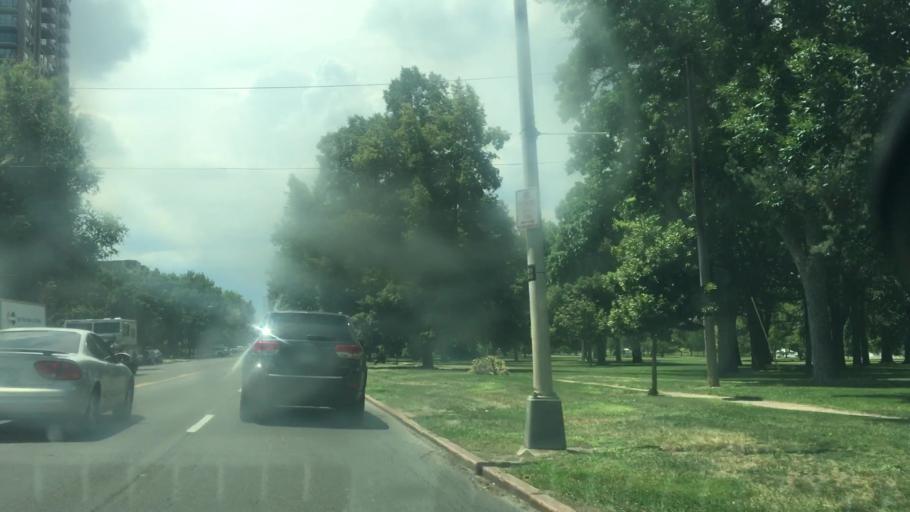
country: US
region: Colorado
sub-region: Denver County
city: Denver
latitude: 39.7439
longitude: -104.9506
